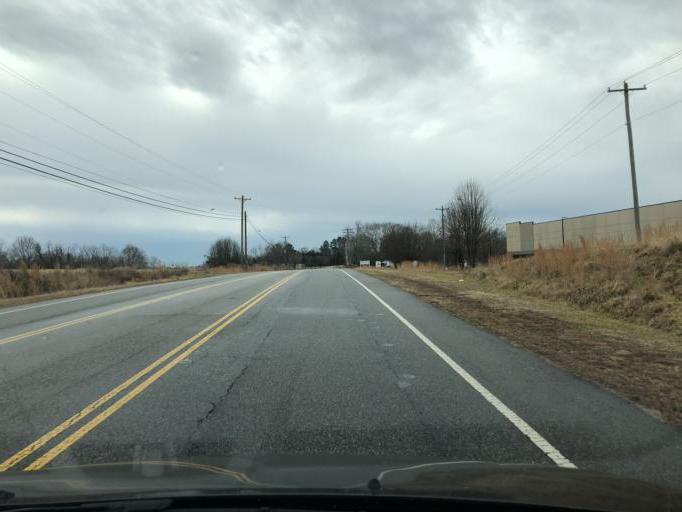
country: US
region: South Carolina
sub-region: Greenville County
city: Greer
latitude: 34.8822
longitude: -82.1953
